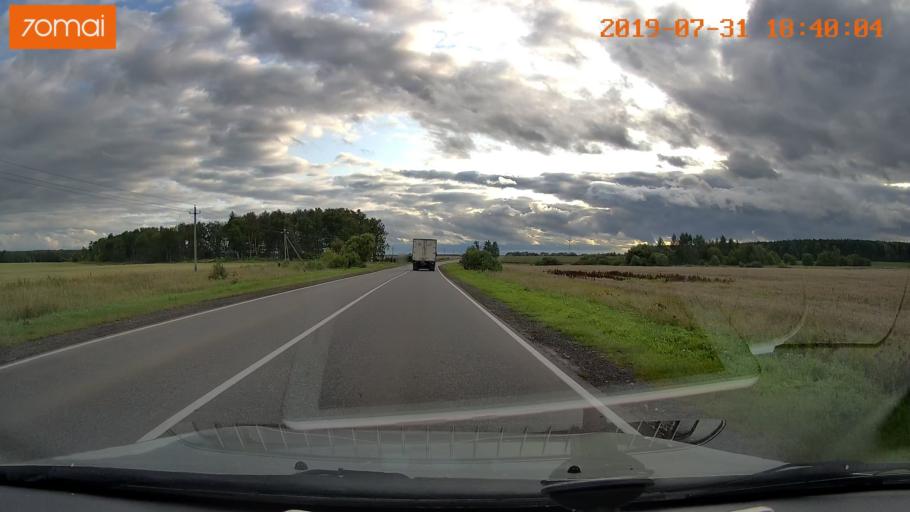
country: RU
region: Moskovskaya
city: Voskresensk
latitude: 55.2633
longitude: 38.6370
